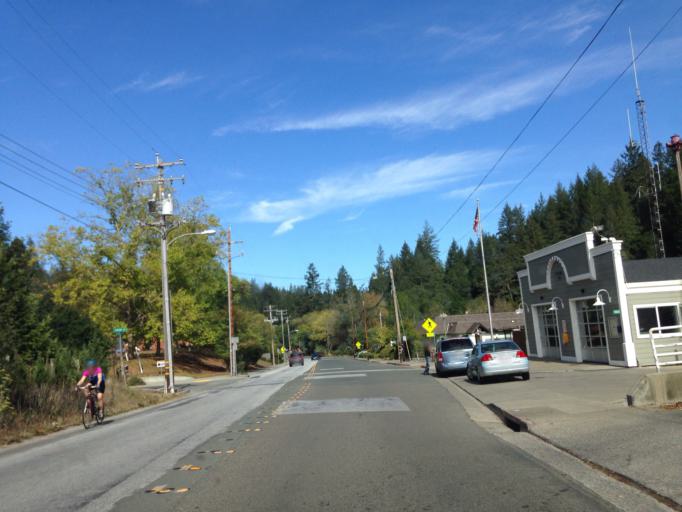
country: US
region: California
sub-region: Sonoma County
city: Occidental
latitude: 38.4090
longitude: -122.9484
